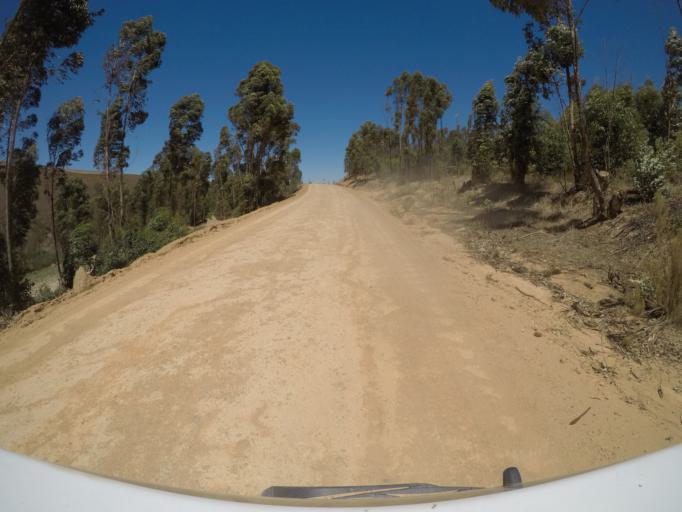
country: ZA
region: Western Cape
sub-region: Overberg District Municipality
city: Grabouw
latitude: -34.2118
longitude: 19.2116
